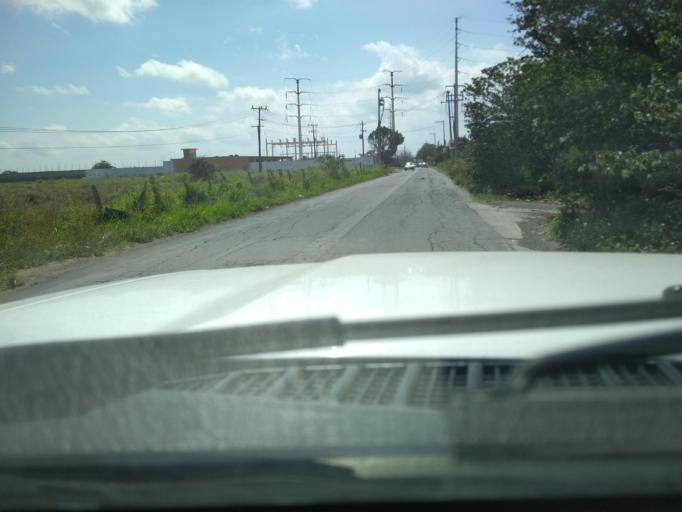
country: MX
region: Veracruz
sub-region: Veracruz
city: Las Amapolas
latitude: 19.1377
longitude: -96.2162
